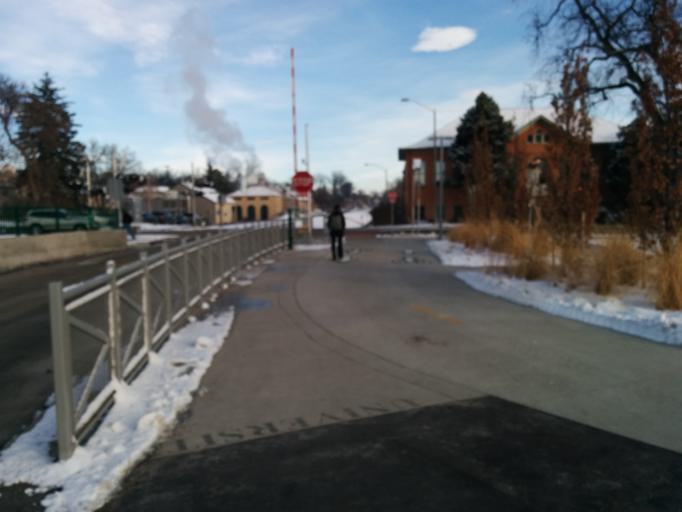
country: US
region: Colorado
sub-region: Larimer County
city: Fort Collins
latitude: 40.5734
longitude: -105.0787
